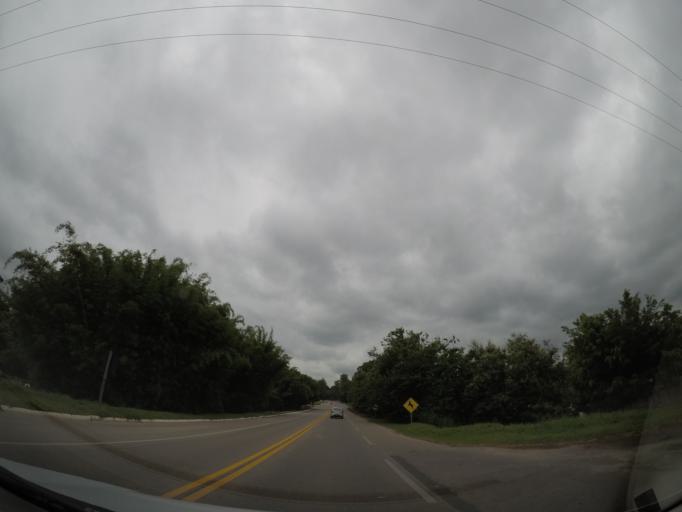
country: BR
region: Sao Paulo
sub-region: Louveira
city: Louveira
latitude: -23.0680
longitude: -46.9503
